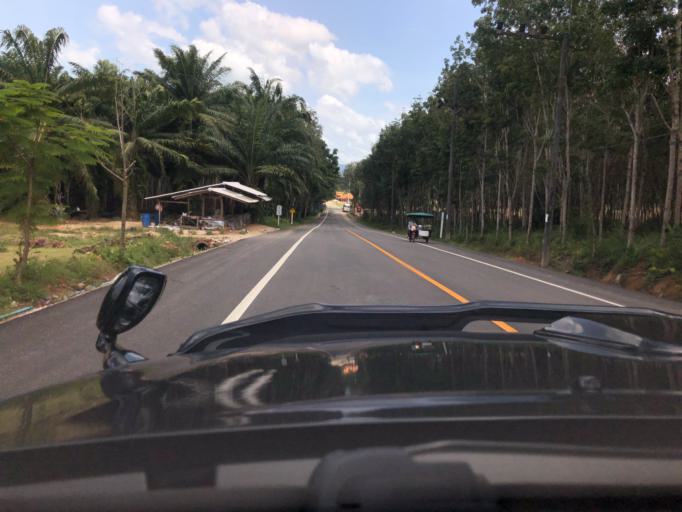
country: TH
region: Krabi
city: Khlong Thom
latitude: 7.9522
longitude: 99.2043
